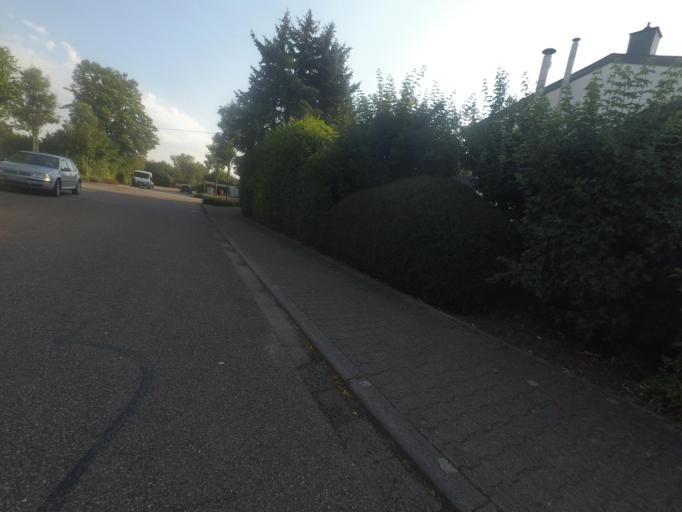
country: DE
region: Baden-Wuerttemberg
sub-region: Karlsruhe Region
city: Sinzheim
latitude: 48.7586
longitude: 8.1631
